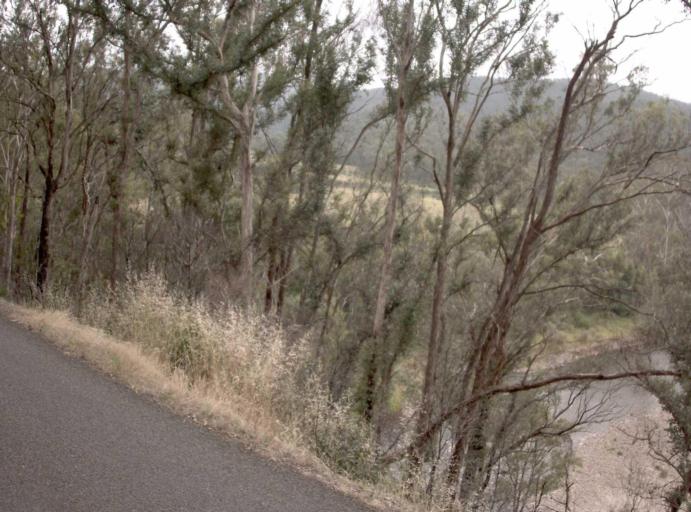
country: AU
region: Victoria
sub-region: Wellington
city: Heyfield
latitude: -37.8091
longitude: 146.6718
